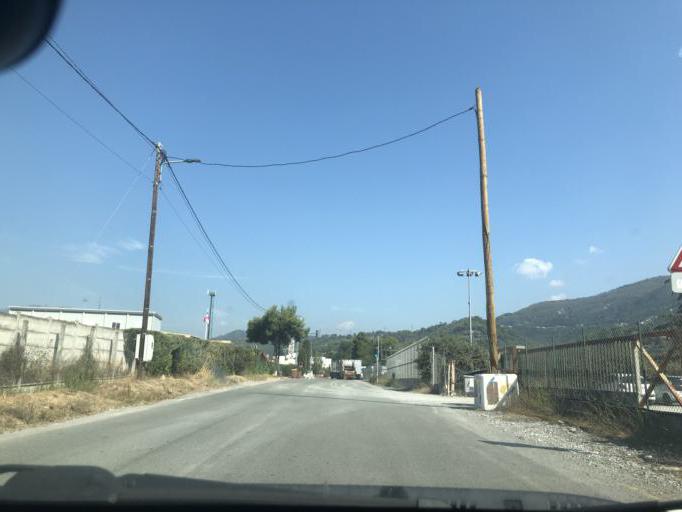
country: FR
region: Provence-Alpes-Cote d'Azur
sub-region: Departement des Alpes-Maritimes
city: Castagniers
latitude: 43.7792
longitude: 7.2107
